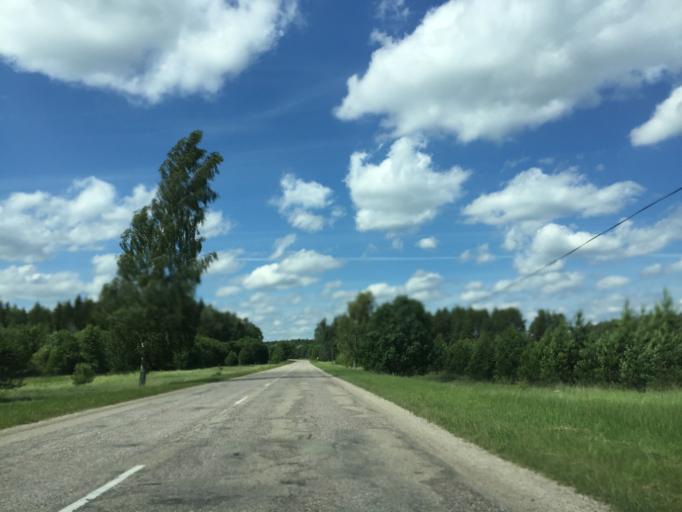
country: LV
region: Engure
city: Smarde
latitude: 56.9733
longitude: 23.3191
